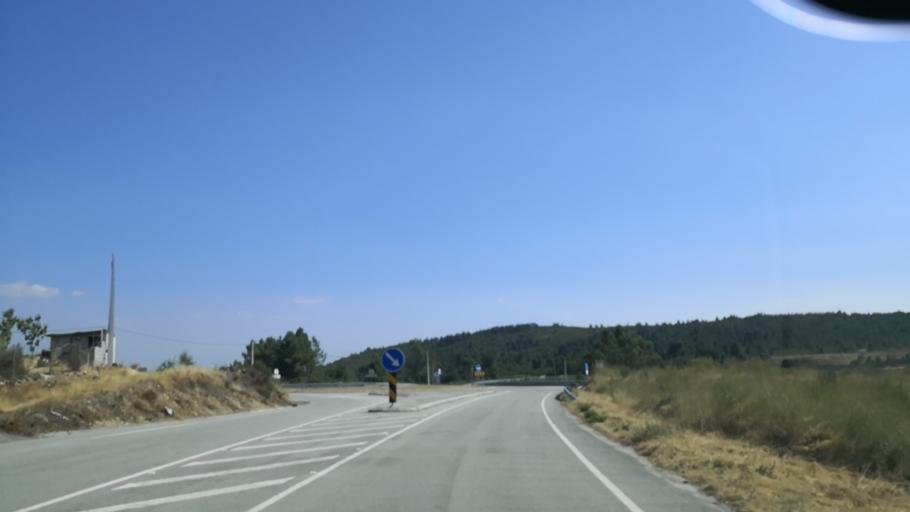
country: PT
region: Vila Real
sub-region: Sabrosa
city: Sabrosa
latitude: 41.3001
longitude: -7.4854
